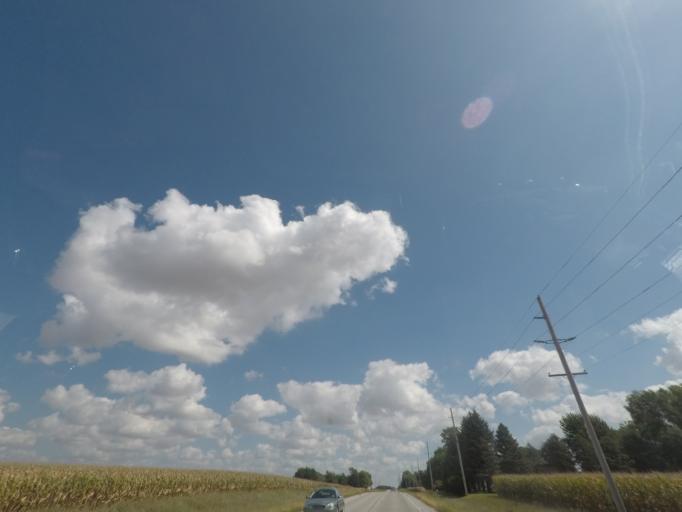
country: US
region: Iowa
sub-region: Story County
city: Nevada
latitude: 42.0227
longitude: -93.4239
